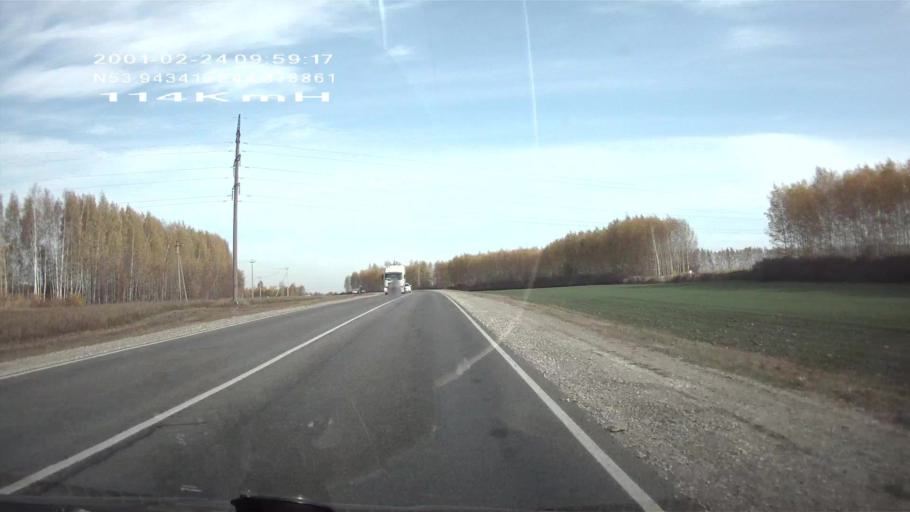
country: RU
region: Penza
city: Issa
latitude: 53.9438
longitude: 44.8792
